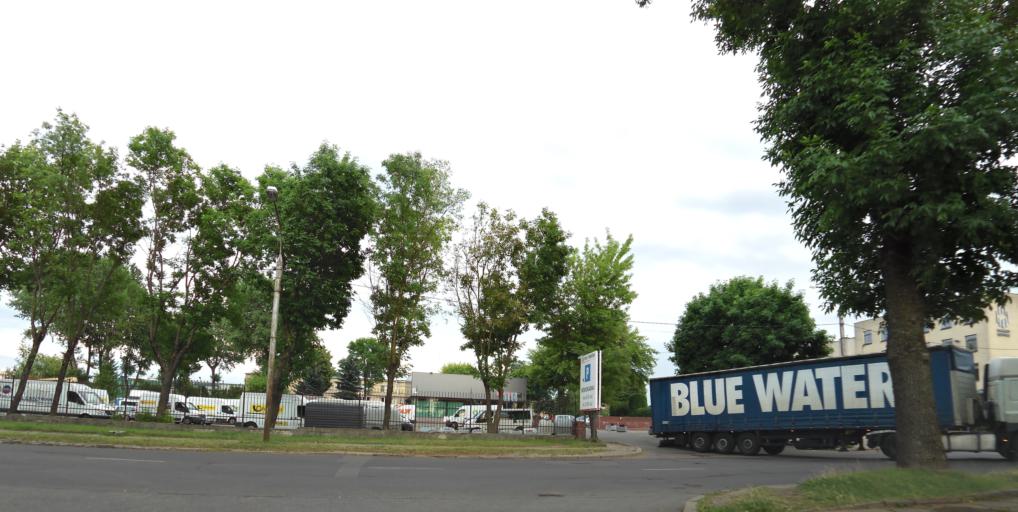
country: LT
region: Vilnius County
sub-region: Vilnius
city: Vilnius
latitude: 54.7146
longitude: 25.2934
